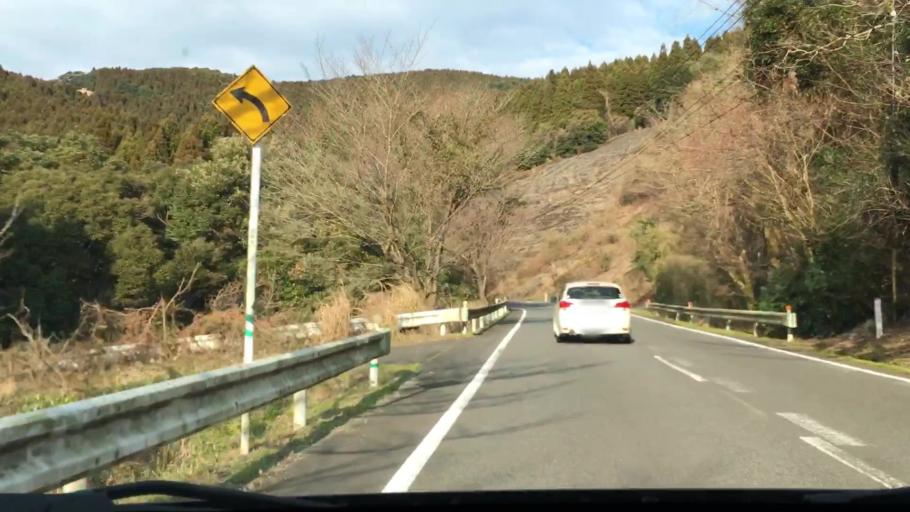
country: JP
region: Miyazaki
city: Miyazaki-shi
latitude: 31.7751
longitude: 131.3324
